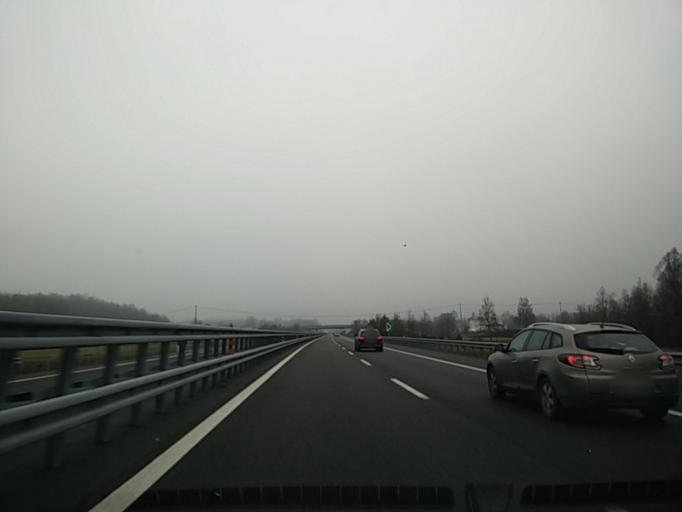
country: IT
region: Piedmont
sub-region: Provincia di Asti
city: Villafranca d'Asti
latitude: 44.9111
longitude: 8.0456
